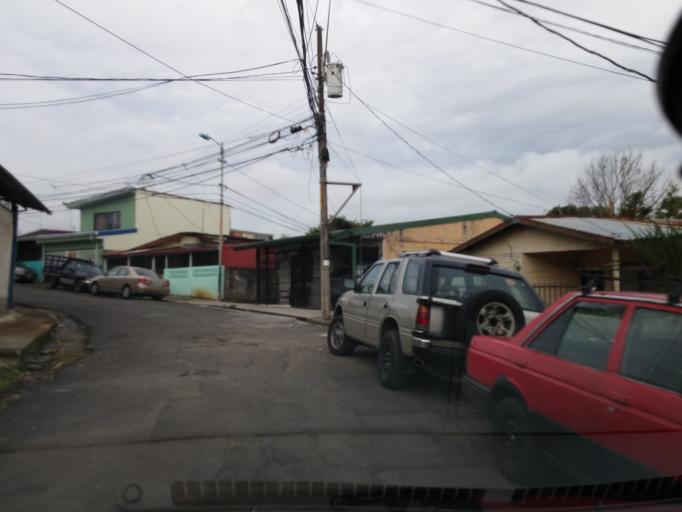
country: CR
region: Heredia
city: Heredia
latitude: 10.0093
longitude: -84.1158
